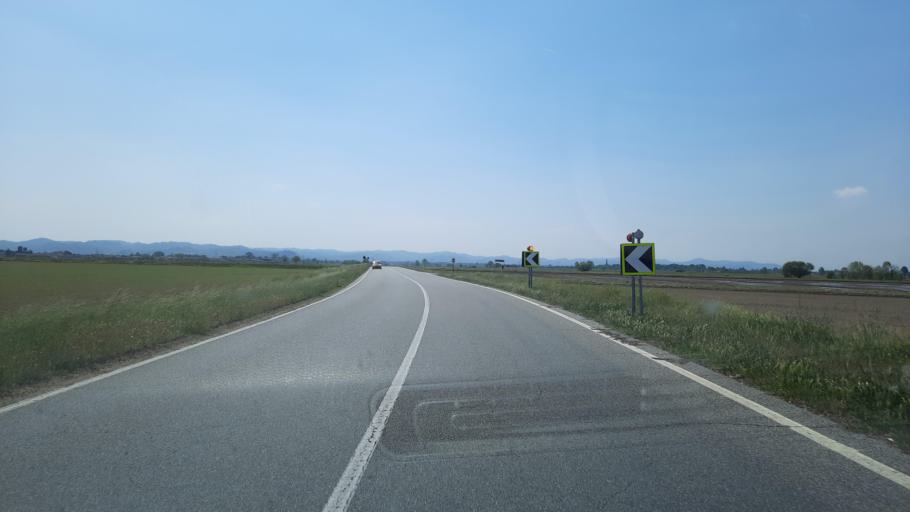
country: IT
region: Piedmont
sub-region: Provincia di Vercelli
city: Lamporo
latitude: 45.2271
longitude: 8.1499
